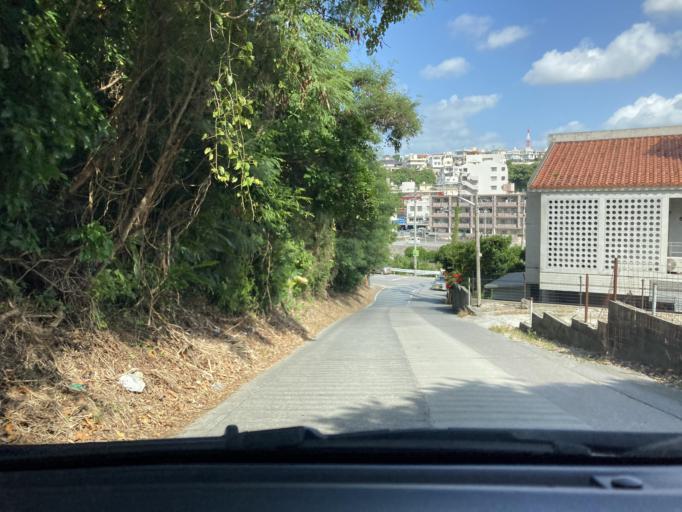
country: JP
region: Okinawa
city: Tomigusuku
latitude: 26.1870
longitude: 127.6851
